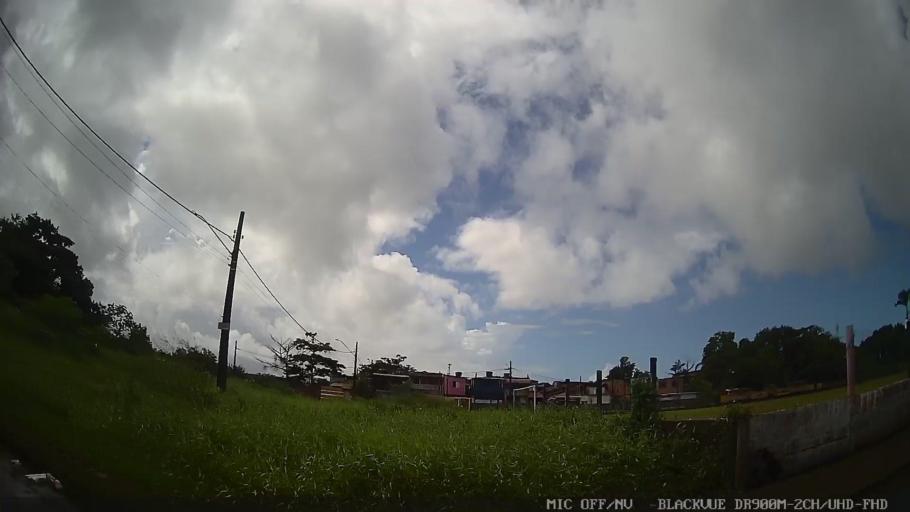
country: BR
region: Sao Paulo
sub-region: Itanhaem
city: Itanhaem
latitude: -24.1961
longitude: -46.8225
